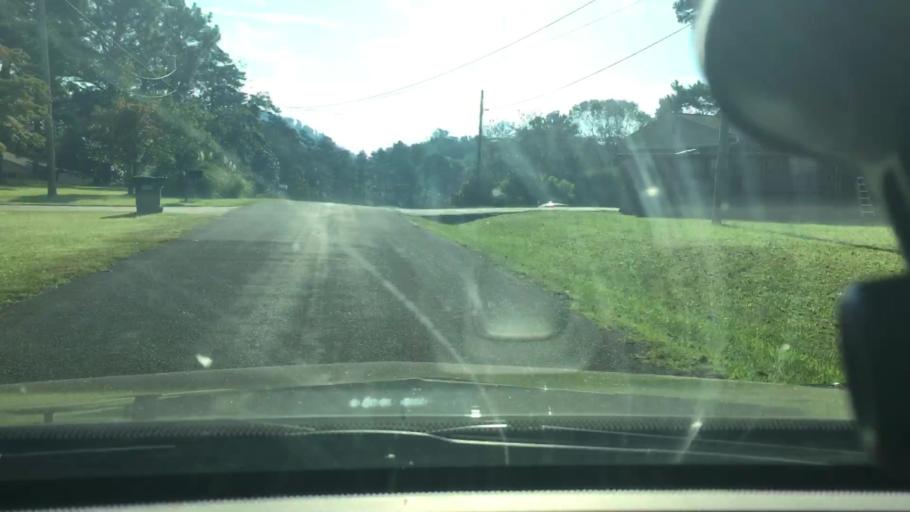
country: US
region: North Carolina
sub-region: Stanly County
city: Badin
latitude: 35.3571
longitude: -80.1189
